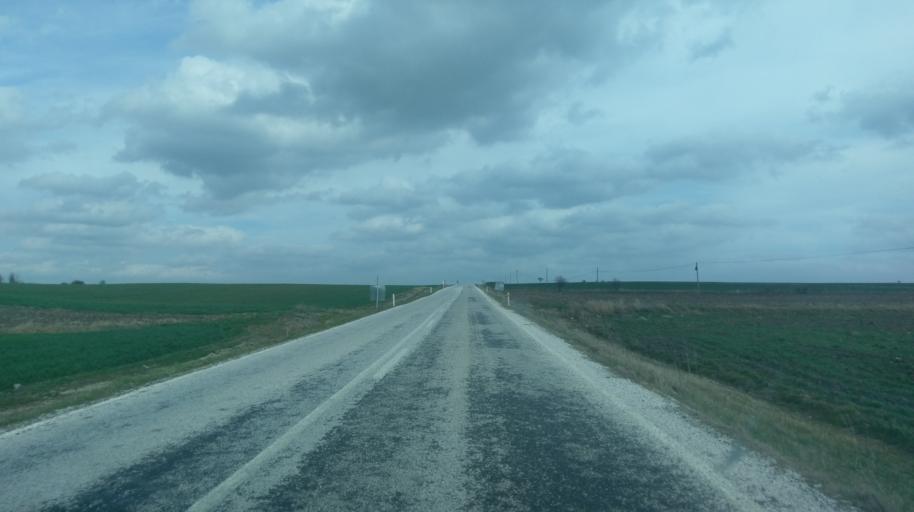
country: TR
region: Edirne
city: Haskoy
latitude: 41.6618
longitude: 26.9350
